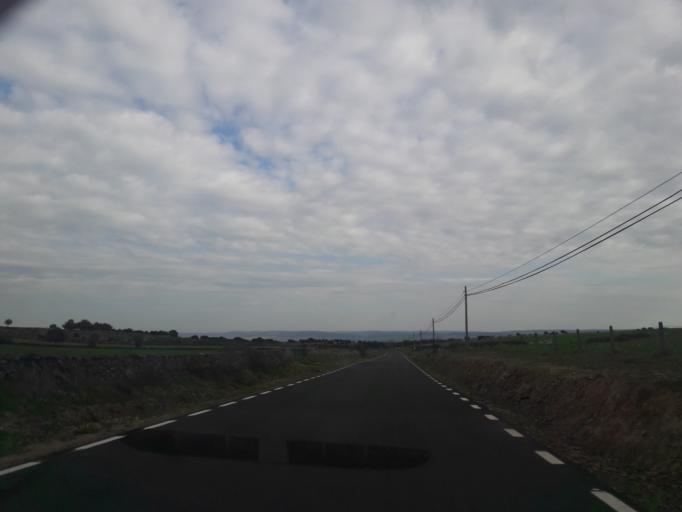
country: ES
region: Castille and Leon
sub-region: Provincia de Salamanca
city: Pastores
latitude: 40.5058
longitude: -6.5294
